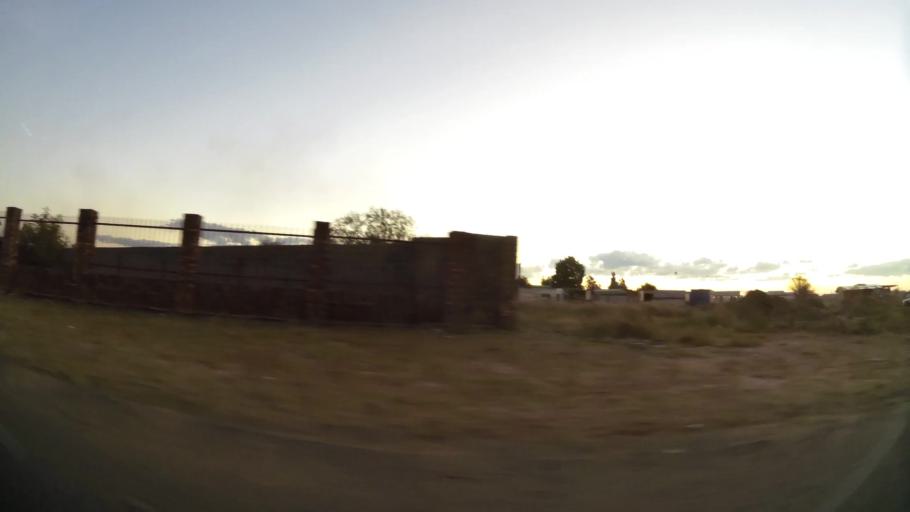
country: ZA
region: Northern Cape
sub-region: Frances Baard District Municipality
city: Kimberley
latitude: -28.7224
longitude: 24.7623
